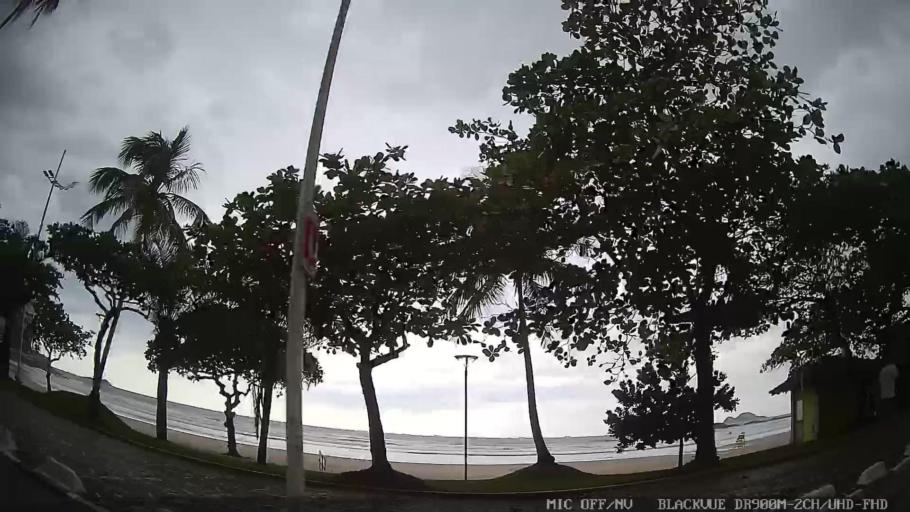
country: BR
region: Sao Paulo
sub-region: Guaruja
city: Guaruja
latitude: -23.9954
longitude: -46.2537
